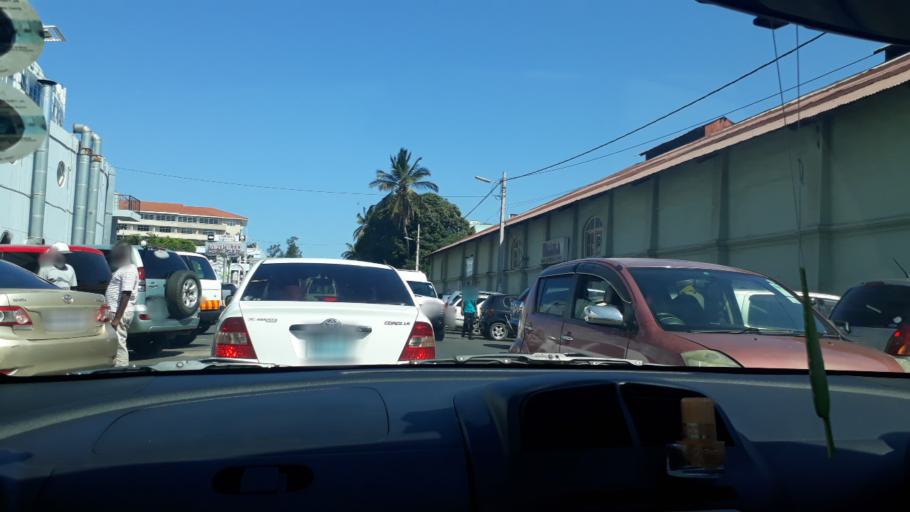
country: MZ
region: Maputo City
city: Maputo
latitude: -25.9761
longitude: 32.5726
